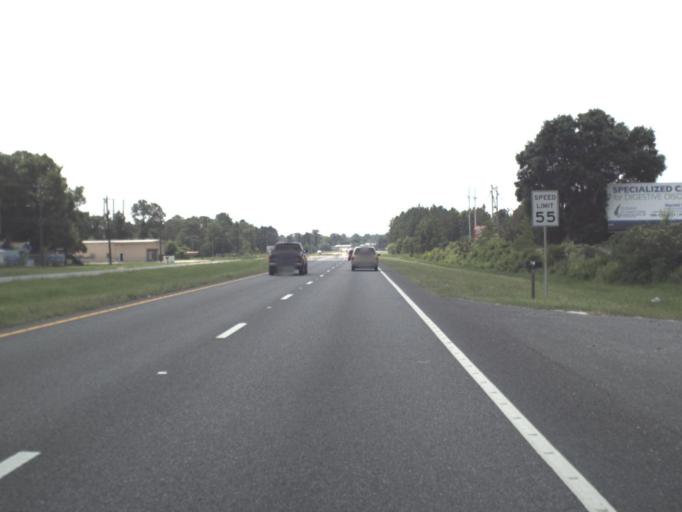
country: US
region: Florida
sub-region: Putnam County
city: Palatka
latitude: 29.6740
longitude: -81.6588
